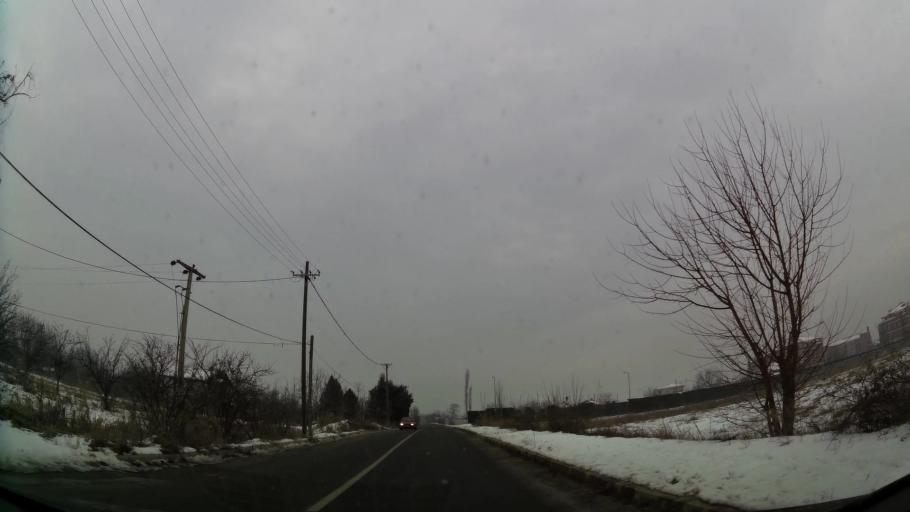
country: MK
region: Cucer-Sandevo
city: Chucher - Sandevo
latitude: 42.0522
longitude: 21.3646
